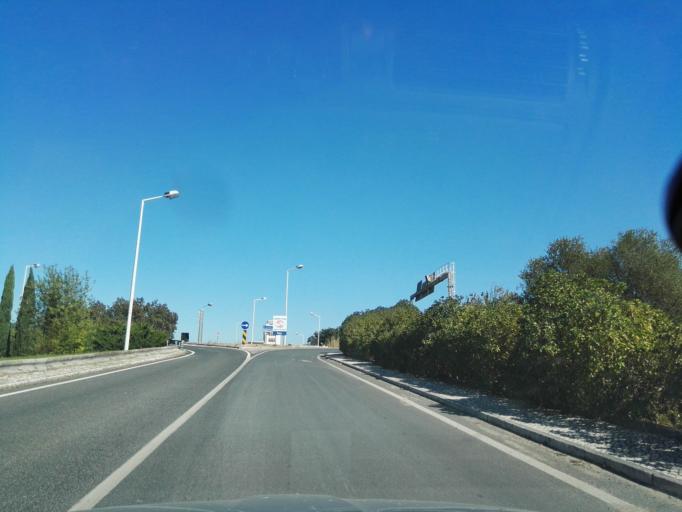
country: PT
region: Lisbon
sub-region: Vila Franca de Xira
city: Vila Franca de Xira
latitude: 38.9600
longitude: -8.9855
